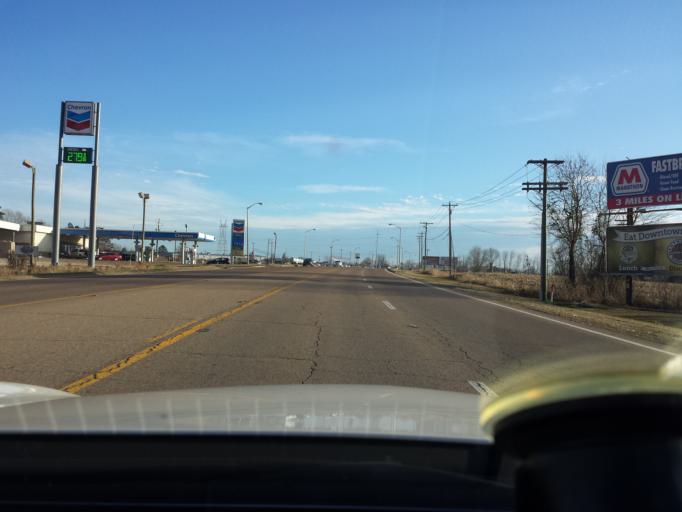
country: US
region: Mississippi
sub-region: Clay County
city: West Point
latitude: 33.6349
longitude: -88.6606
